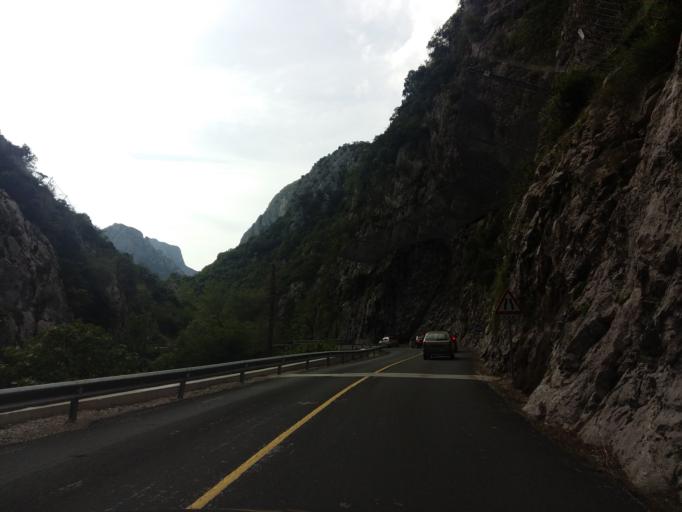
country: ES
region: Cantabria
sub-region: Provincia de Cantabria
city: Tresviso
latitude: 43.2469
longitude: -4.5893
